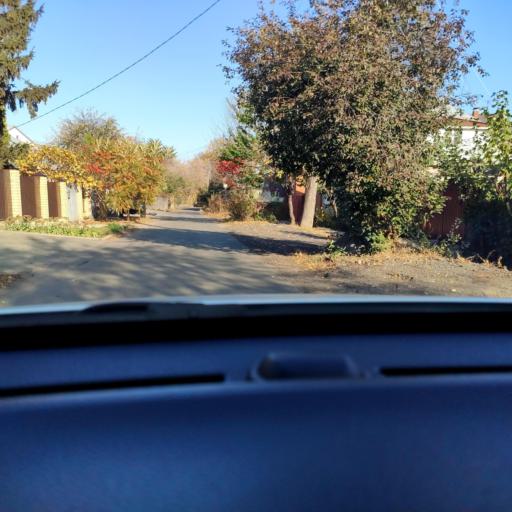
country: RU
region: Voronezj
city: Voronezh
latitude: 51.6968
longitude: 39.2141
